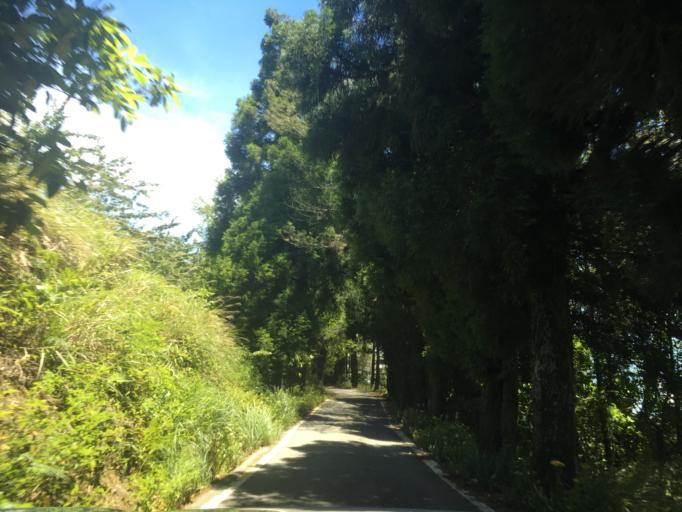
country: TW
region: Taiwan
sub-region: Nantou
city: Puli
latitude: 24.2278
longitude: 121.2430
